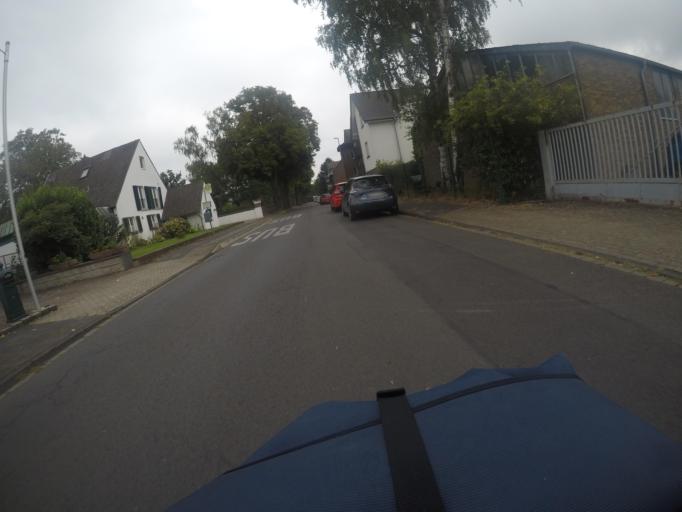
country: DE
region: North Rhine-Westphalia
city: Tonisvorst
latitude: 51.3792
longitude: 6.5055
